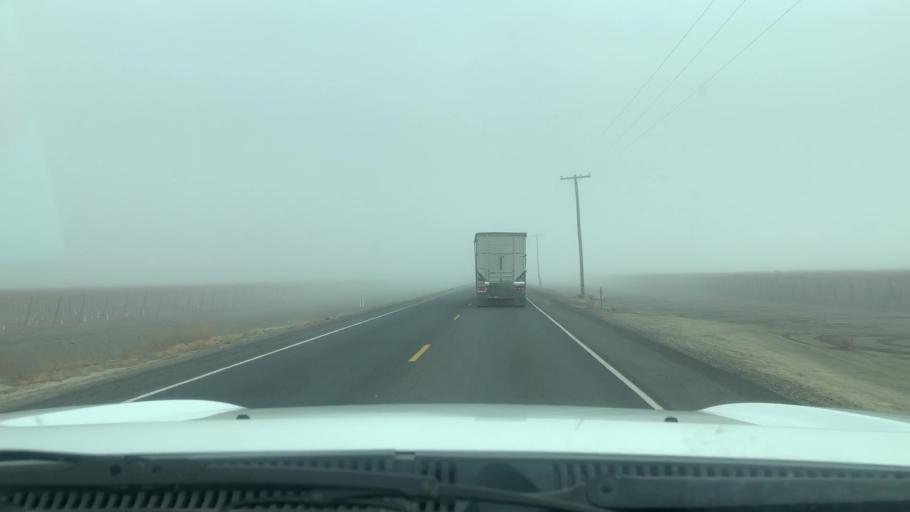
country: US
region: California
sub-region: Kern County
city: Buttonwillow
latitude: 35.4993
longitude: -119.5898
